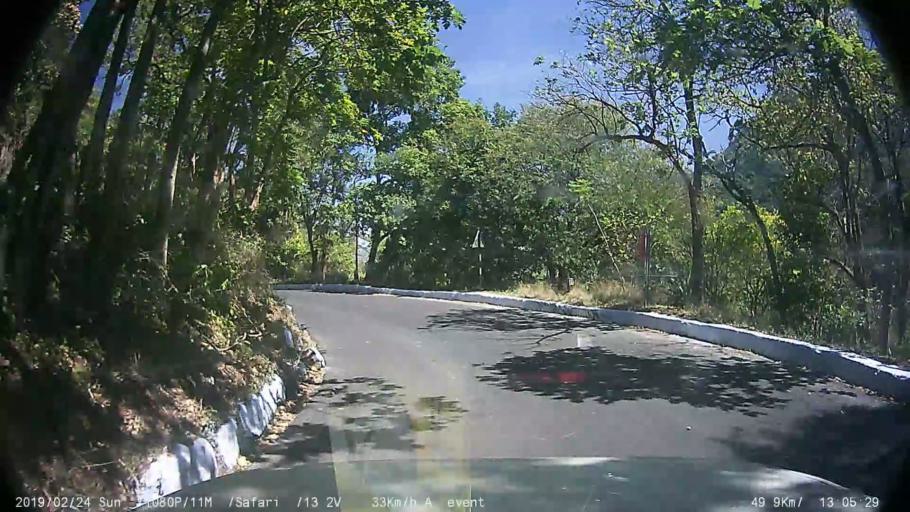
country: IN
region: Tamil Nadu
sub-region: Nilgiri
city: Wellington
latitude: 11.3342
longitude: 76.8270
